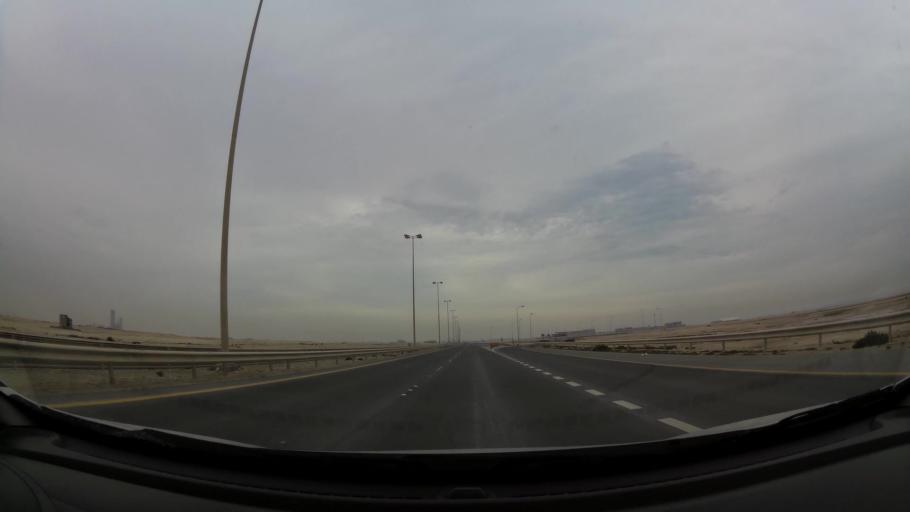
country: BH
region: Central Governorate
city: Dar Kulayb
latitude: 26.0205
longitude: 50.6074
